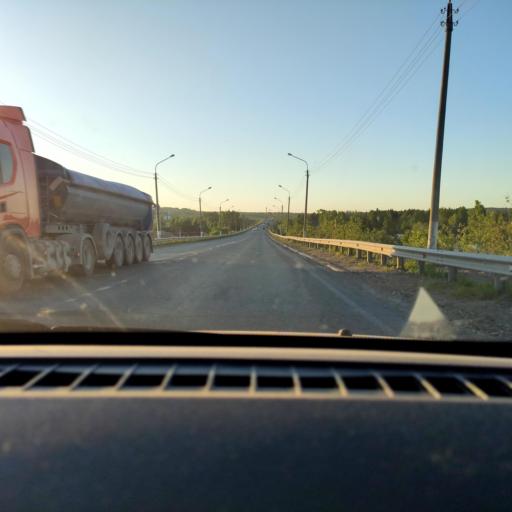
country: RU
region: Perm
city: Polazna
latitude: 58.1724
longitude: 56.4148
